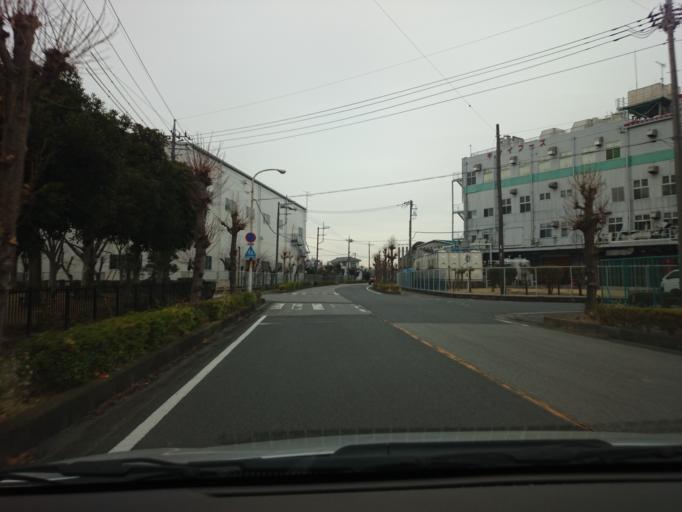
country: JP
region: Saitama
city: Kisai
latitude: 36.1123
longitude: 139.5678
